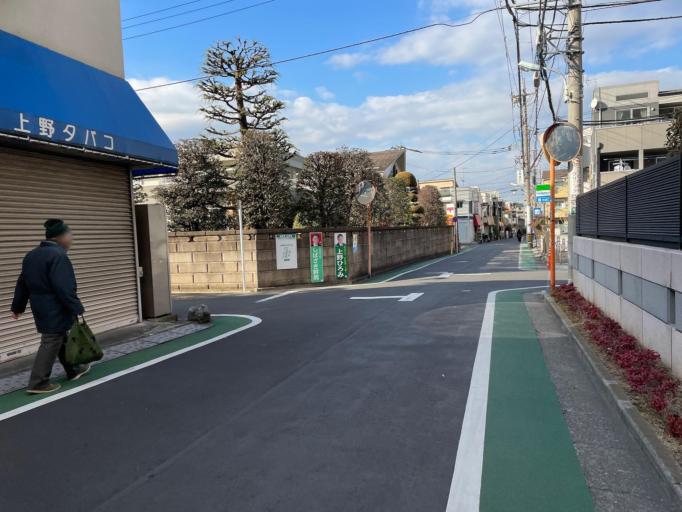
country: JP
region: Saitama
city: Wako
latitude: 35.7614
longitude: 139.6495
